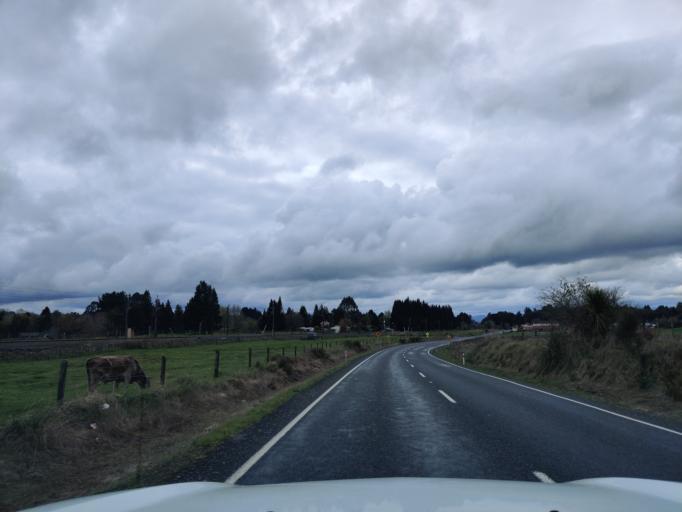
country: NZ
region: Waikato
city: Turangi
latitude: -39.0047
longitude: 175.3767
